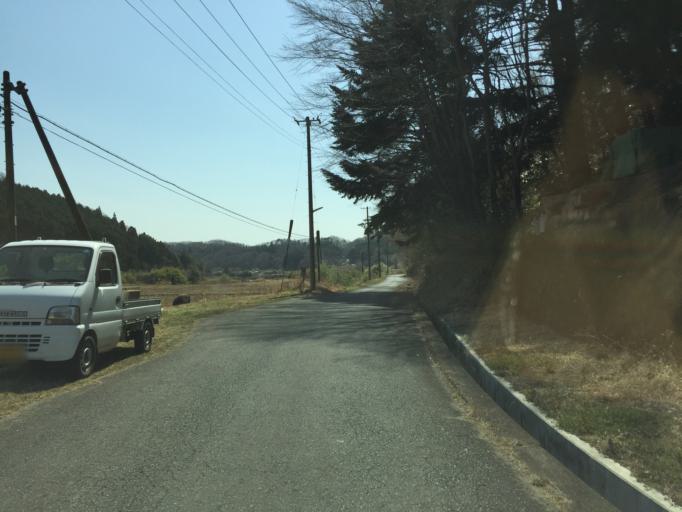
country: JP
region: Fukushima
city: Iwaki
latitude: 37.0066
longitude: 140.7941
